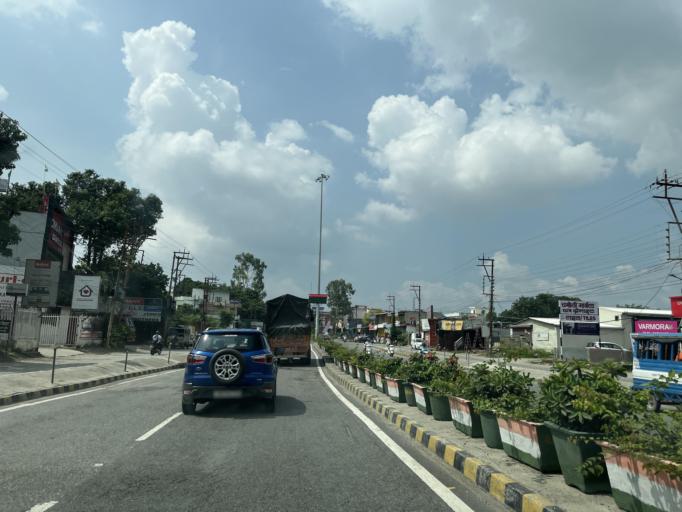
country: IN
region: Uttarakhand
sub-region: Dehradun
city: Raipur
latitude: 30.2797
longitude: 78.0725
